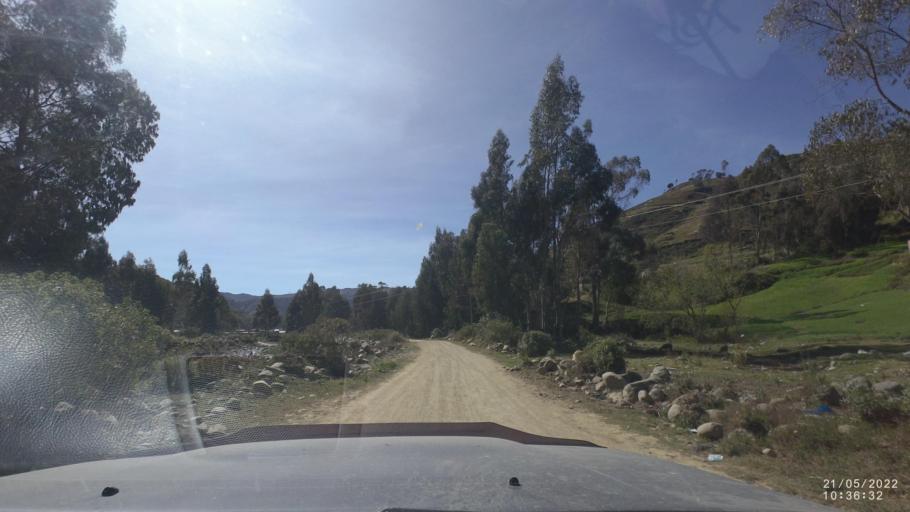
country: BO
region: Cochabamba
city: Colomi
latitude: -17.3143
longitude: -65.9225
